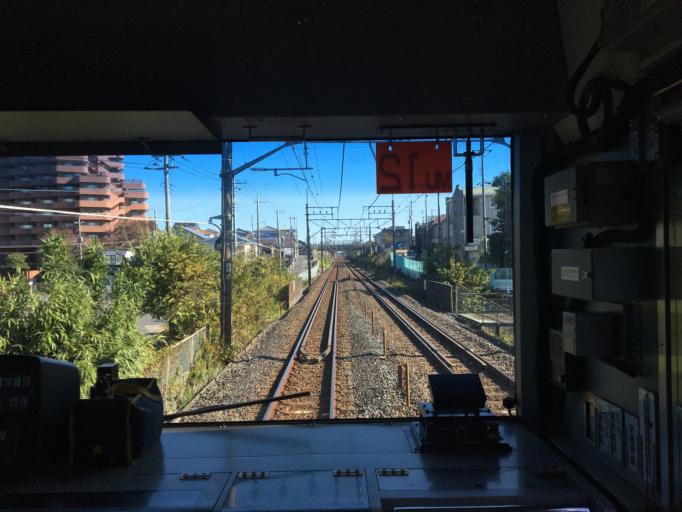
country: JP
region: Saitama
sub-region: Kawaguchi-shi
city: Hatogaya-honcho
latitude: 35.8715
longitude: 139.7245
